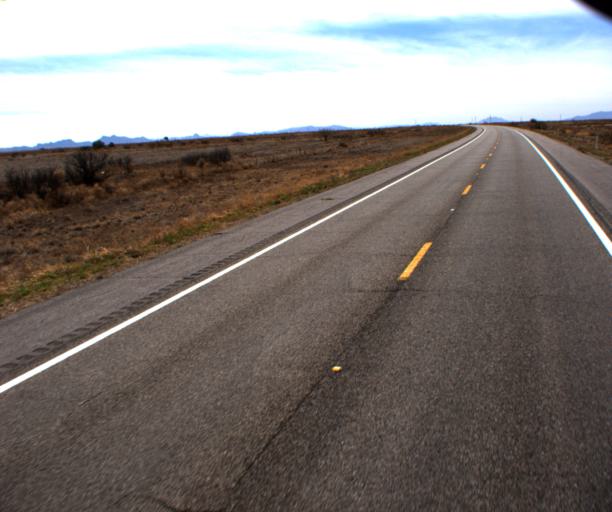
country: US
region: Arizona
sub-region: Cochise County
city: Pirtleville
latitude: 31.5617
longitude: -109.6671
